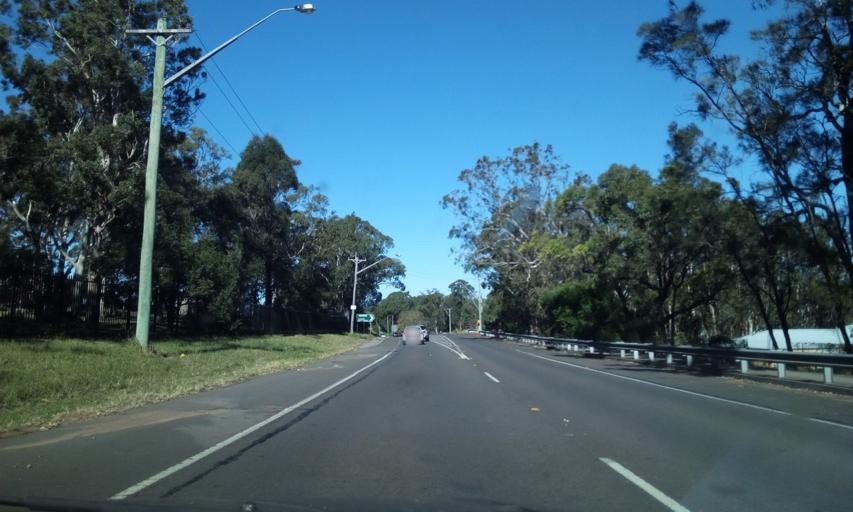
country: AU
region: New South Wales
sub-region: Wollongong
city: Dapto
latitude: -34.5152
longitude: 150.7840
